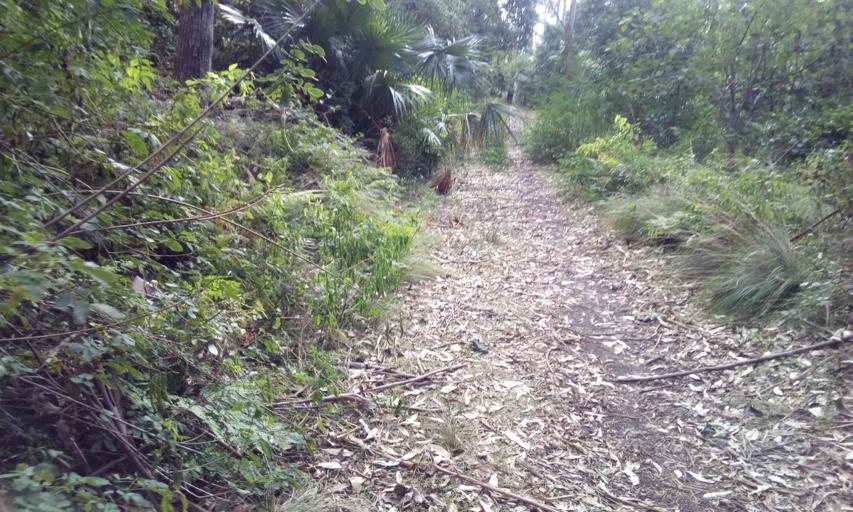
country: AU
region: New South Wales
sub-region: Wollongong
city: Cordeaux Heights
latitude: -34.4396
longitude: 150.8134
